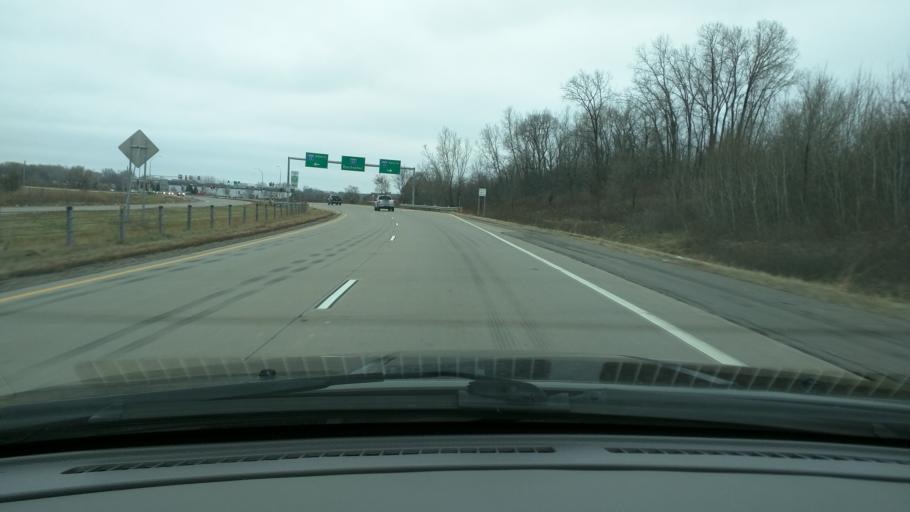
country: US
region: Minnesota
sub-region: Dakota County
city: Mendota Heights
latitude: 44.8762
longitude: -93.1640
